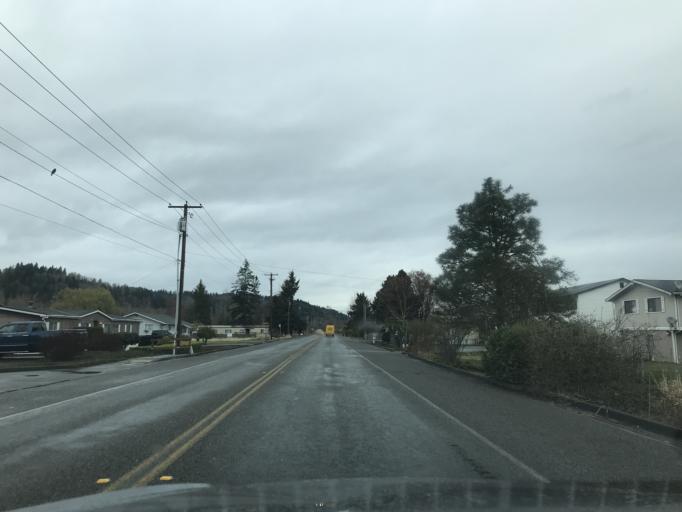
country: US
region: Washington
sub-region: King County
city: Algona
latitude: 47.2902
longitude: -122.2551
